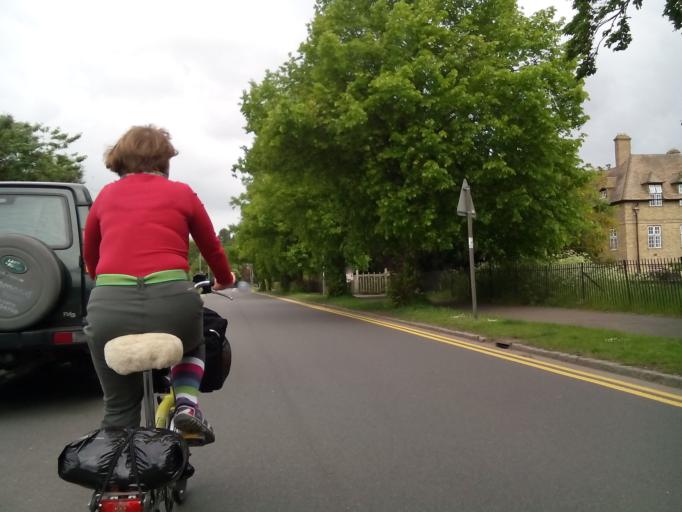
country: GB
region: England
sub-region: Northamptonshire
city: Oundle
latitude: 52.4840
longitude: -0.4707
